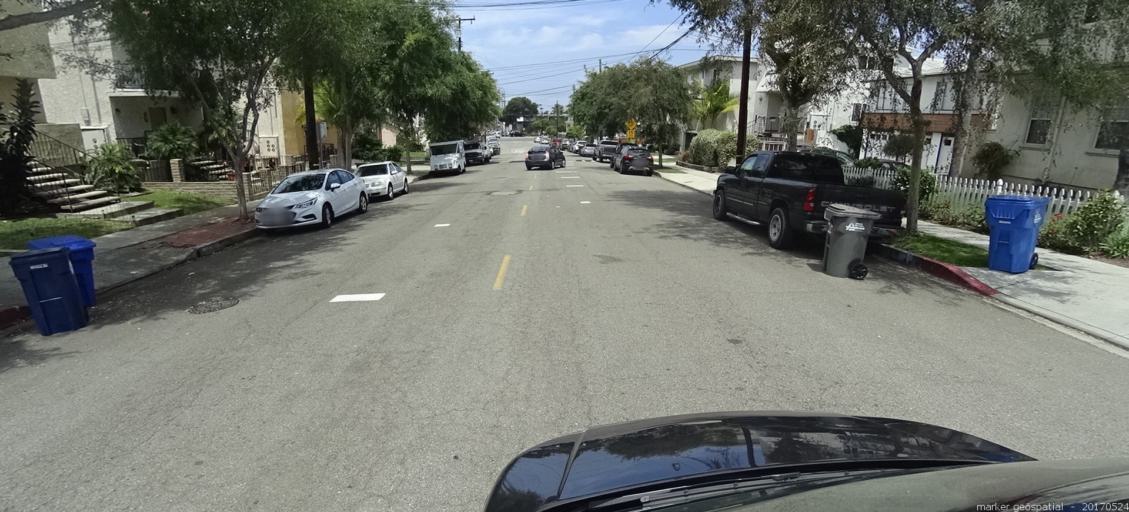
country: US
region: California
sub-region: Los Angeles County
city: Redondo Beach
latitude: 33.8490
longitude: -118.3902
